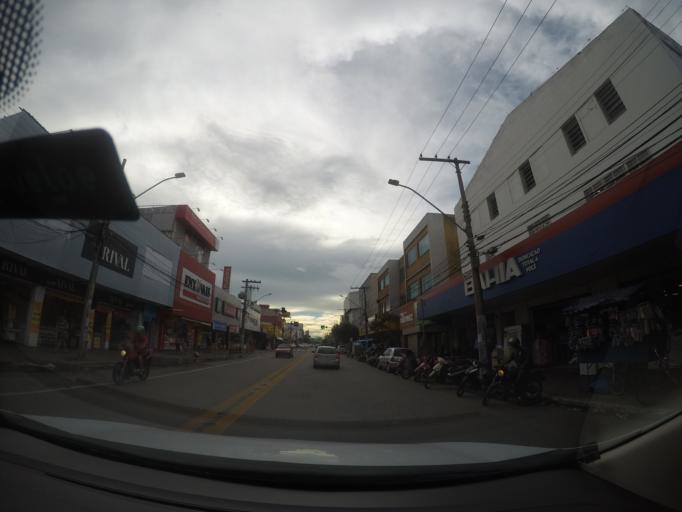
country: BR
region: Goias
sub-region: Goiania
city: Goiania
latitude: -16.6689
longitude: -49.2914
